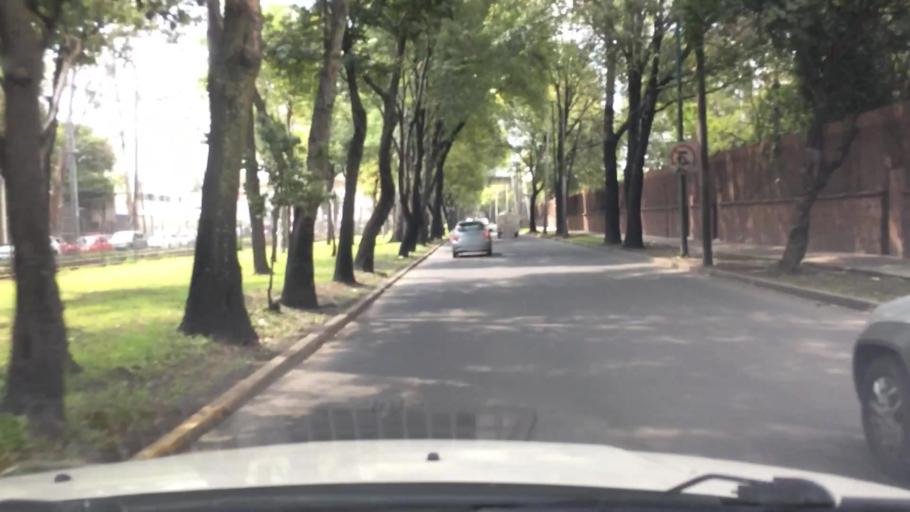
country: MX
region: Mexico City
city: Tlalpan
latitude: 19.2839
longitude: -99.1408
